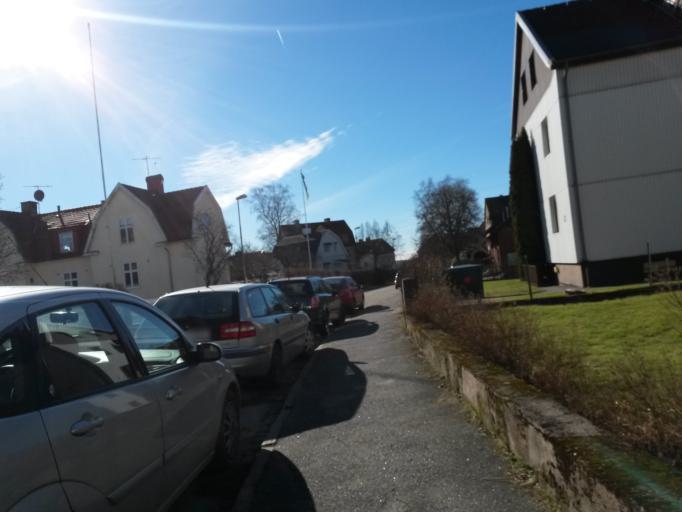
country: SE
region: Vaestra Goetaland
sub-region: Boras Kommun
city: Boras
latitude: 57.7309
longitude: 12.9466
